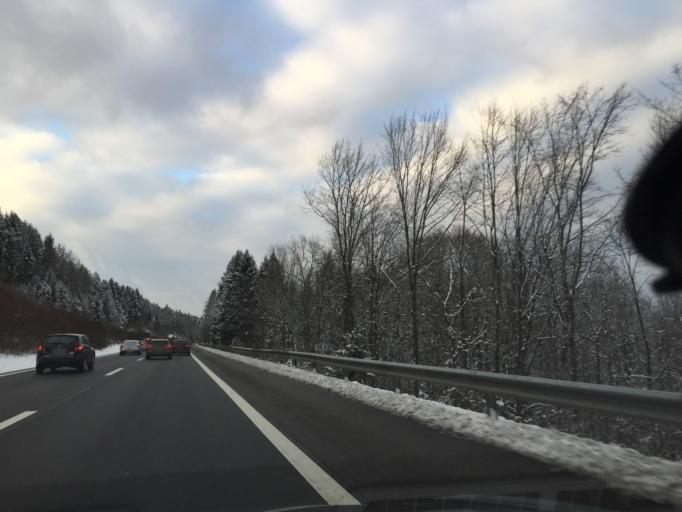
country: CH
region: Zurich
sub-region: Bezirk Horgen
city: Horgen / Oberdorf
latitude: 47.2562
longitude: 8.5859
